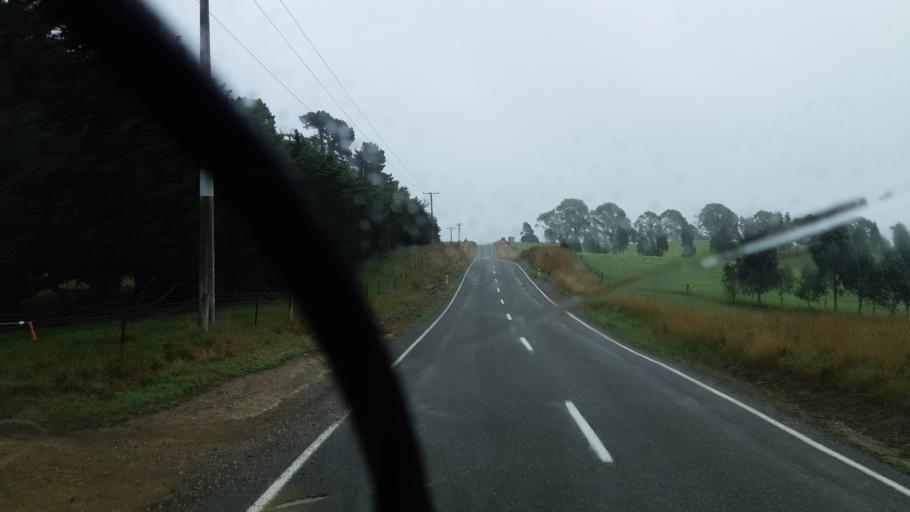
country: NZ
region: Otago
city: Oamaru
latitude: -44.9375
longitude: 170.7672
